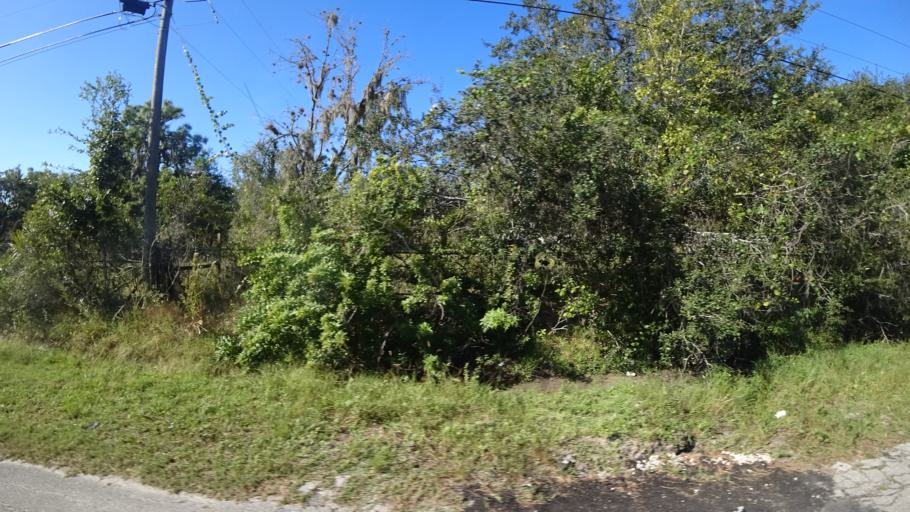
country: US
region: Florida
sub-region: Hillsborough County
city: Sun City Center
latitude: 27.6523
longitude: -82.3557
